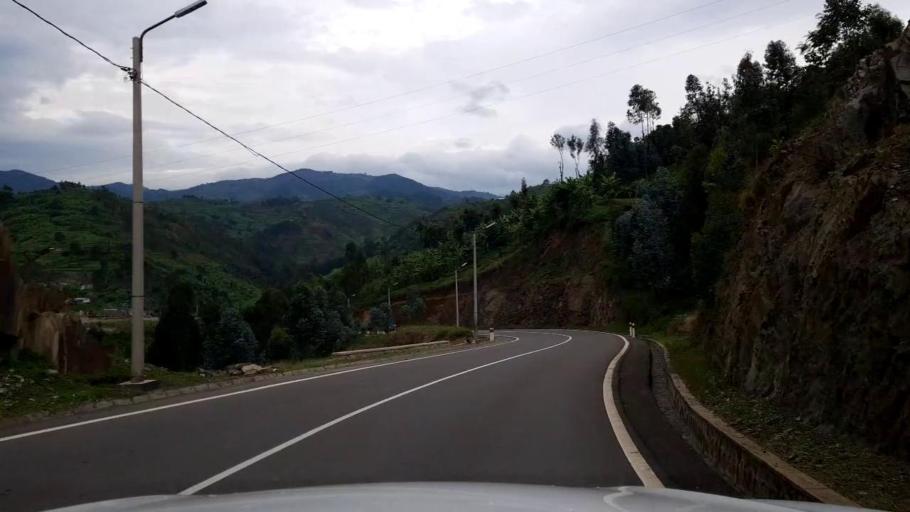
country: RW
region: Western Province
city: Kibuye
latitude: -2.0347
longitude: 29.3976
